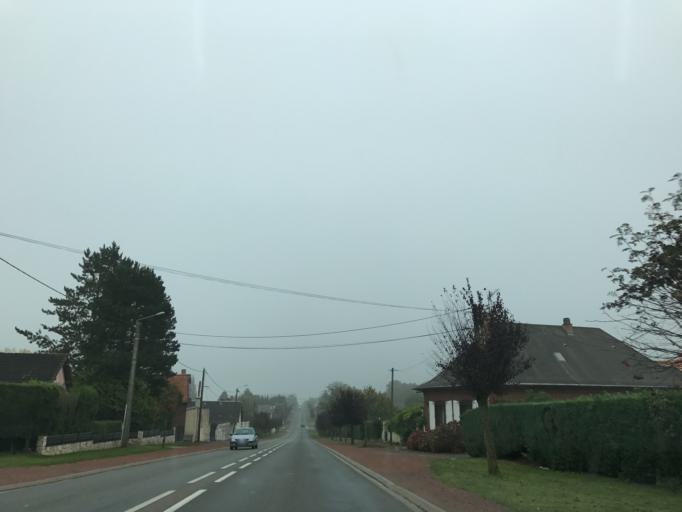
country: FR
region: Nord-Pas-de-Calais
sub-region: Departement du Pas-de-Calais
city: Bapaume
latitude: 50.0805
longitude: 2.8779
